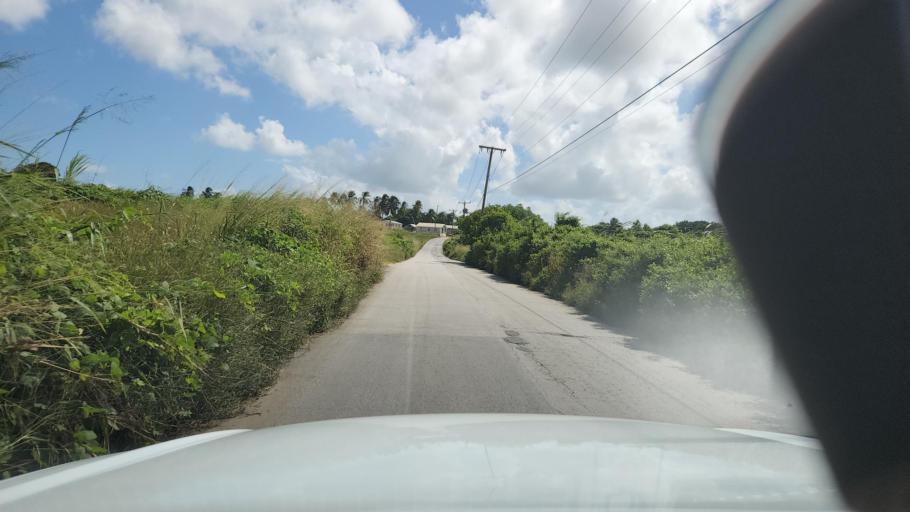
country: BB
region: Saint John
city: Four Cross Roads
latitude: 13.1662
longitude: -59.4842
